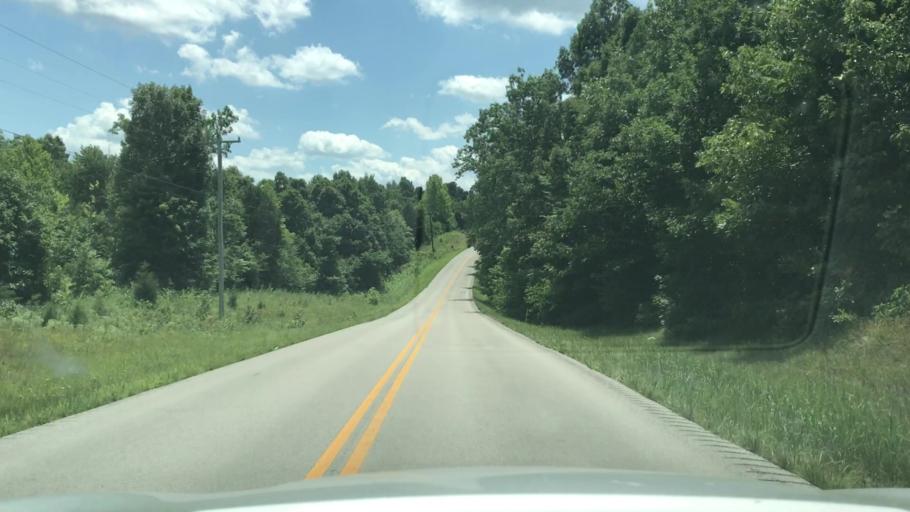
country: US
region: Kentucky
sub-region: Hopkins County
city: Nortonville
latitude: 37.1087
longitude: -87.3344
